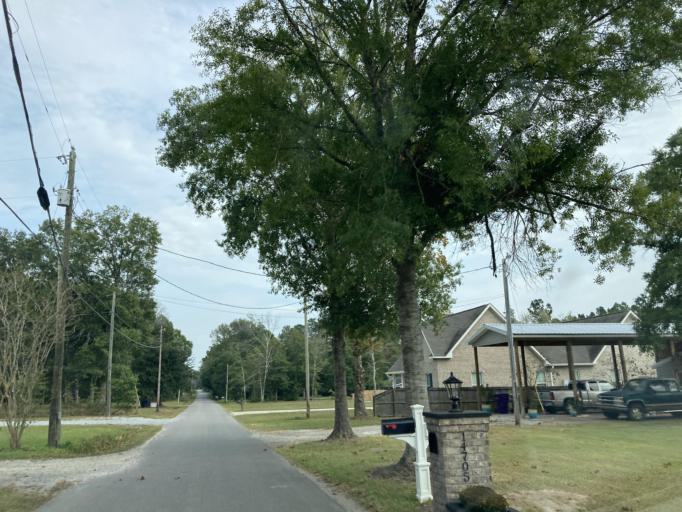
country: US
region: Mississippi
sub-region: Jackson County
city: Saint Martin
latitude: 30.4666
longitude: -88.8548
